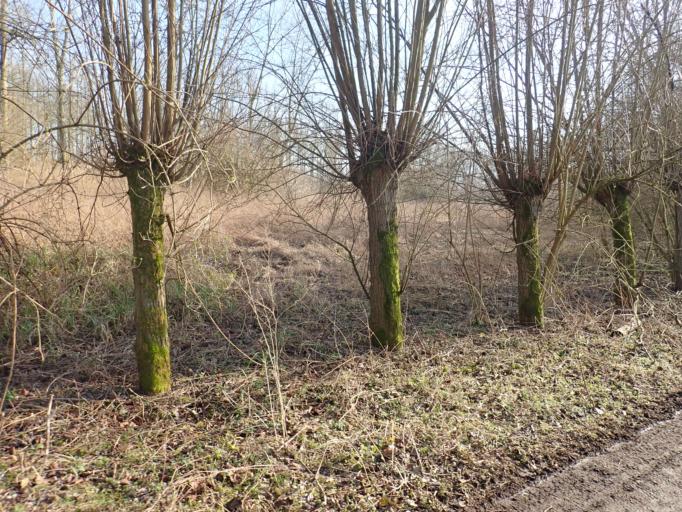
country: BE
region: Flanders
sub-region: Provincie Oost-Vlaanderen
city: Hamme
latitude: 51.0541
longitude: 4.1466
